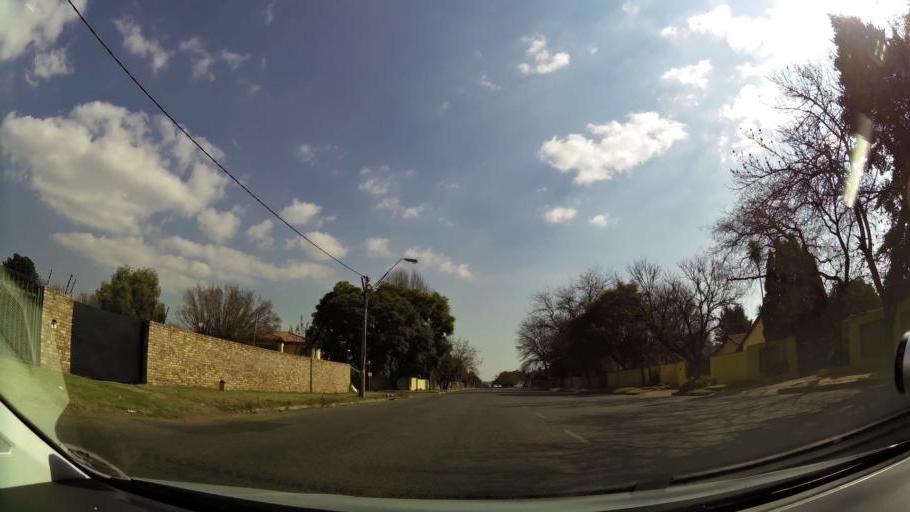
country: ZA
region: Gauteng
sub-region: City of Johannesburg Metropolitan Municipality
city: Modderfontein
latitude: -26.0924
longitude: 28.2410
